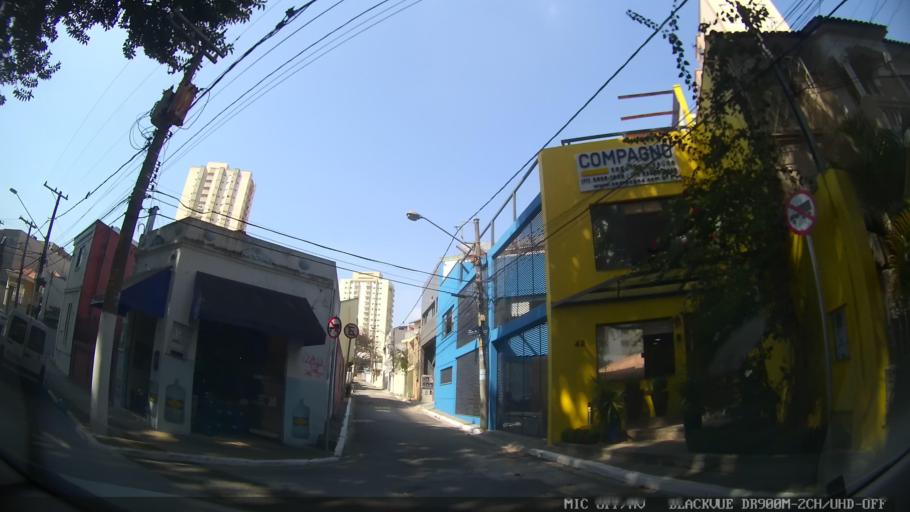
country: BR
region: Sao Paulo
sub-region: Sao Paulo
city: Sao Paulo
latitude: -23.4924
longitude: -46.6277
